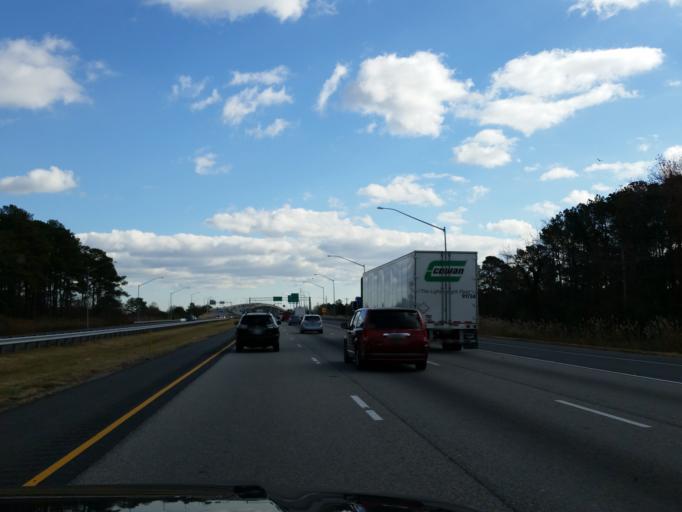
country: US
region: Maryland
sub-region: Queen Anne's County
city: Chester
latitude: 38.9732
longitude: -76.2619
